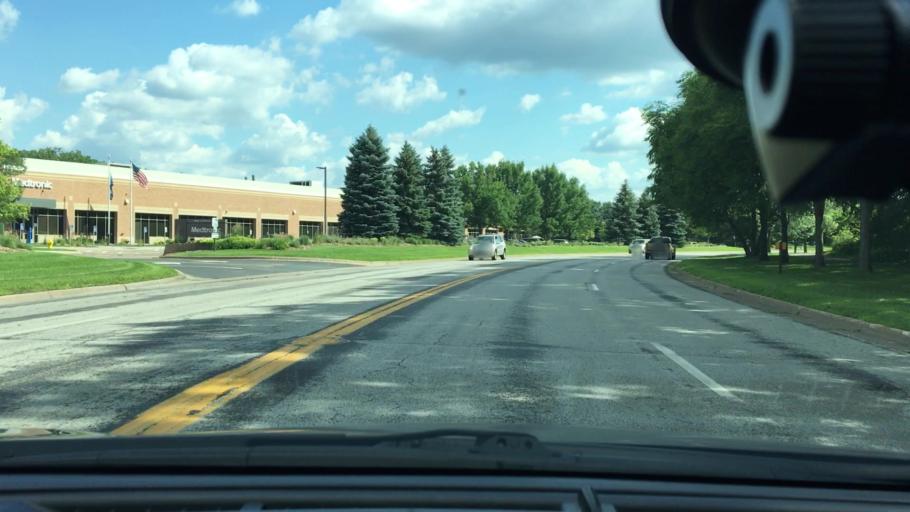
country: US
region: Minnesota
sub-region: Hennepin County
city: New Hope
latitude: 45.0400
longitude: -93.4051
